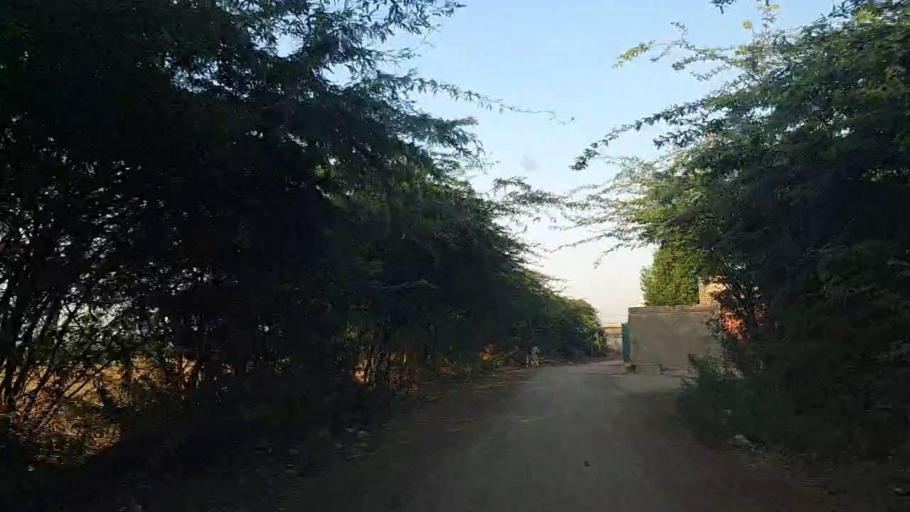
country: PK
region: Sindh
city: Thatta
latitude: 24.7581
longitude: 67.9342
